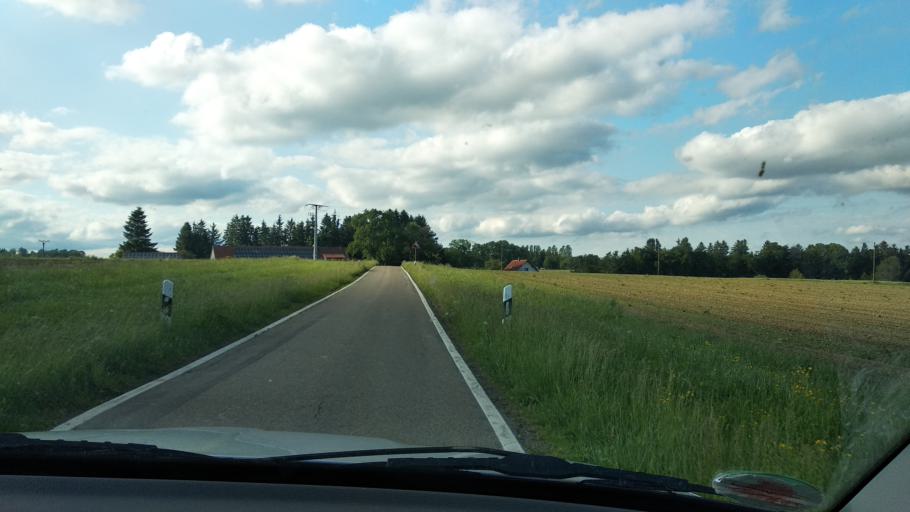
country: DE
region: Baden-Wuerttemberg
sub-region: Tuebingen Region
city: Aitrach
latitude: 47.9446
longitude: 10.0435
